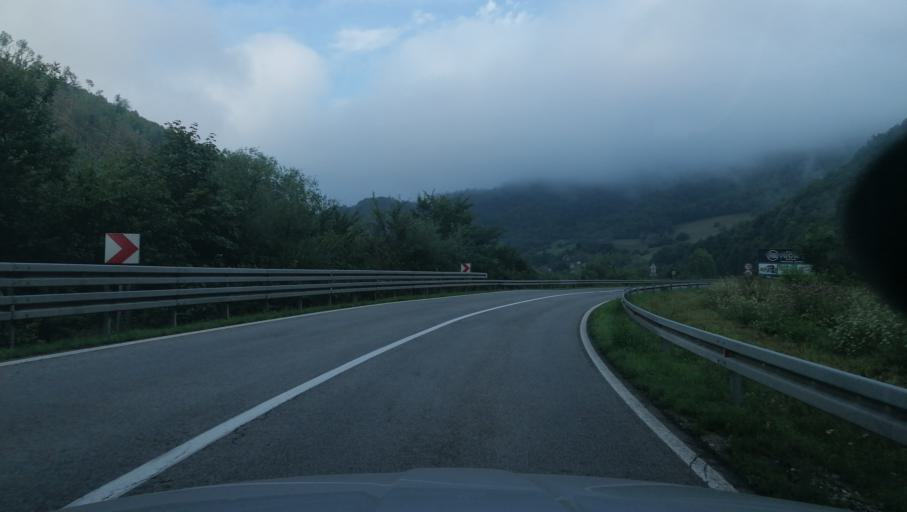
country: BA
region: Federation of Bosnia and Herzegovina
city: Donji Vakuf
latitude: 44.1872
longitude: 17.3425
